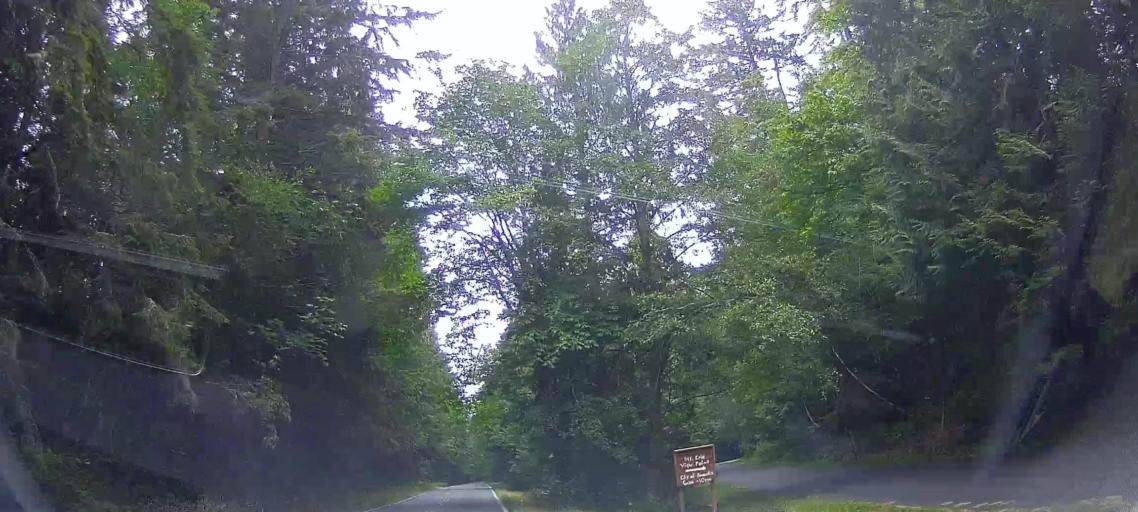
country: US
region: Washington
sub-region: Skagit County
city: Anacortes
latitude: 48.4667
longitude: -122.6312
